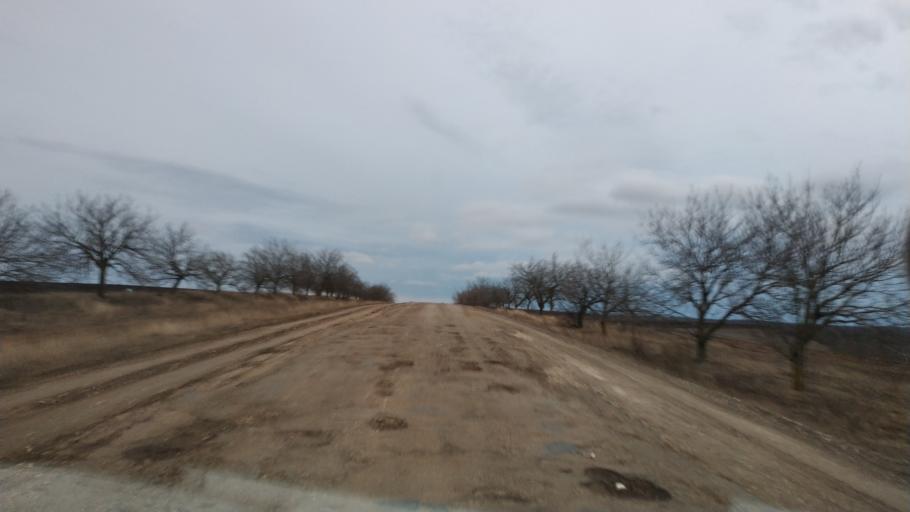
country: MD
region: Causeni
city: Causeni
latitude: 46.5750
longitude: 29.3894
